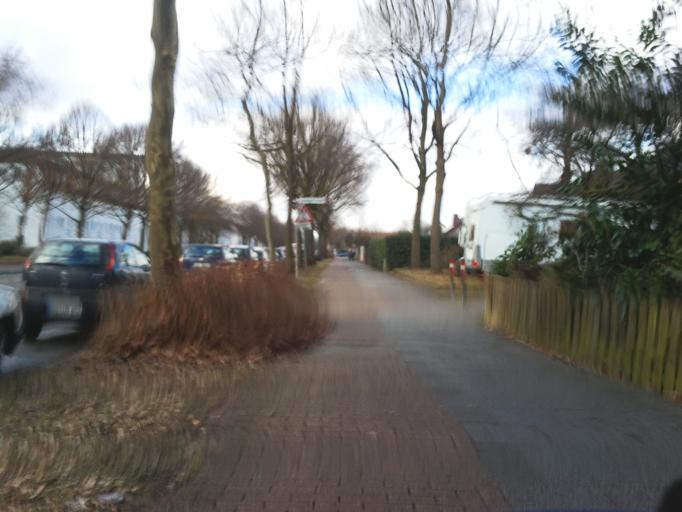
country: DE
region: Bremen
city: Bremen
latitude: 53.0965
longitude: 8.8192
